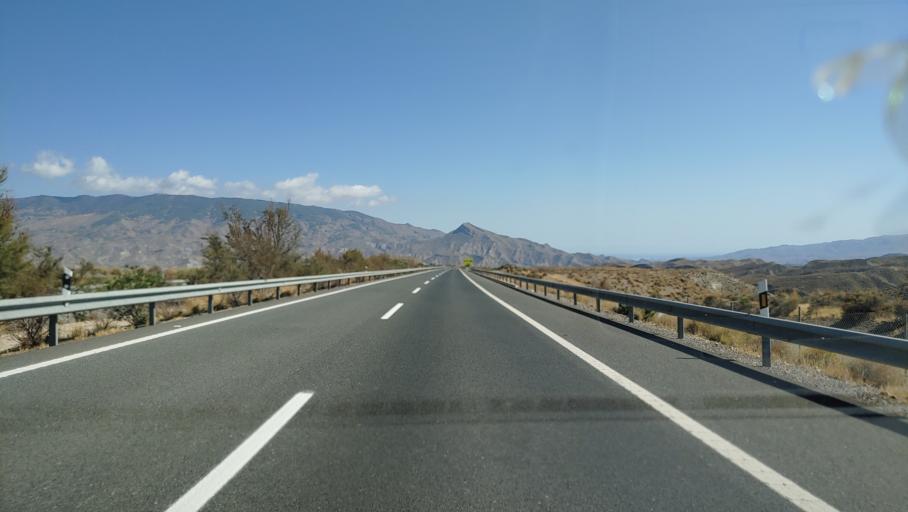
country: ES
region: Andalusia
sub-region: Provincia de Almeria
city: Tabernas
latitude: 37.0534
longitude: -2.4764
